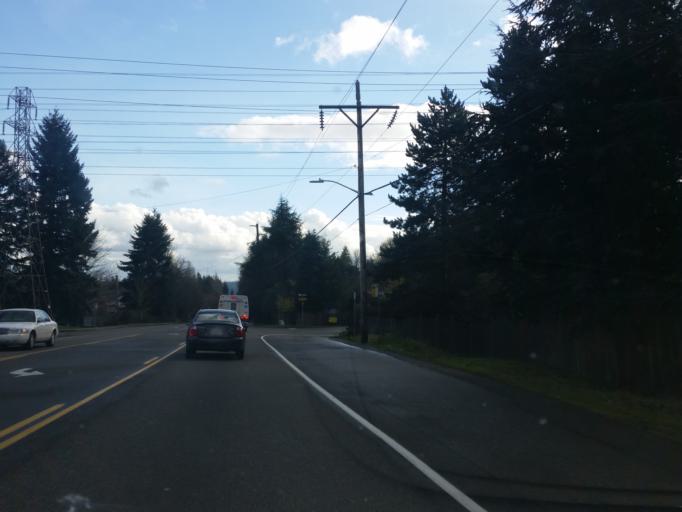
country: US
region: Washington
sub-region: Snohomish County
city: Mountlake Terrace
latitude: 47.7727
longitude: -122.3067
